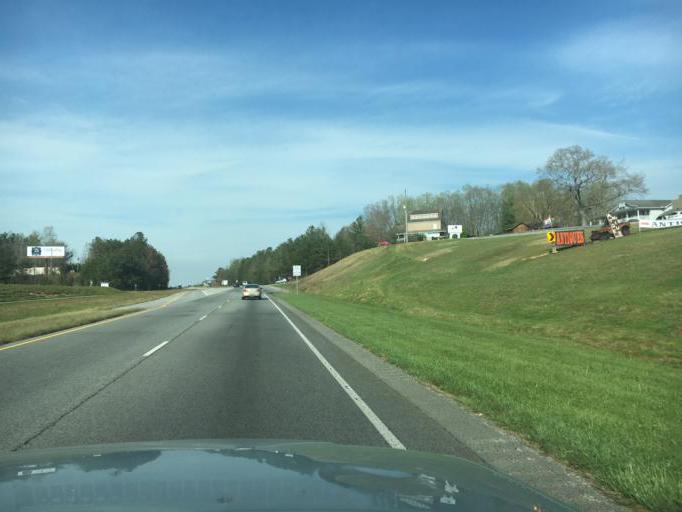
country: US
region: Georgia
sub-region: Banks County
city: Alto
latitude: 34.4750
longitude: -83.5920
